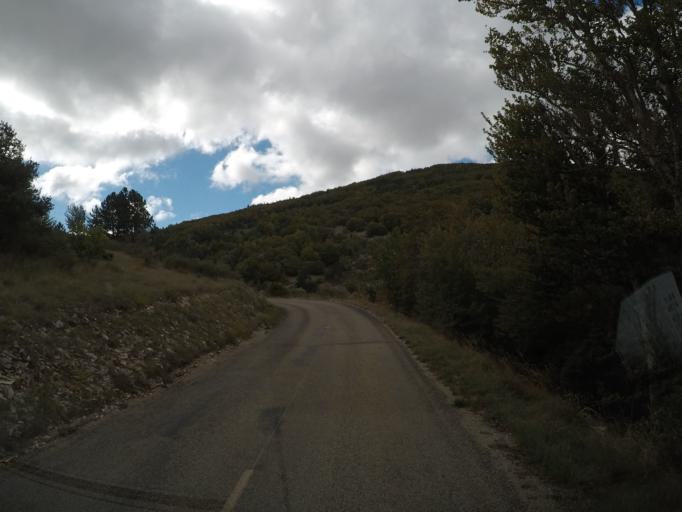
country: FR
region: Provence-Alpes-Cote d'Azur
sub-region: Departement du Vaucluse
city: Sault
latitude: 44.1664
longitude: 5.4968
